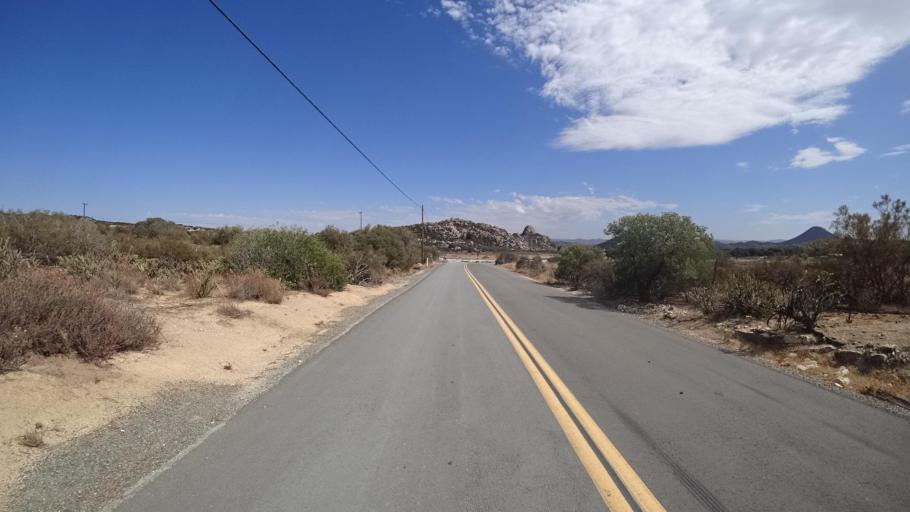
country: MX
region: Baja California
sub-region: Tecate
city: Cereso del Hongo
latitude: 32.6409
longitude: -116.2739
